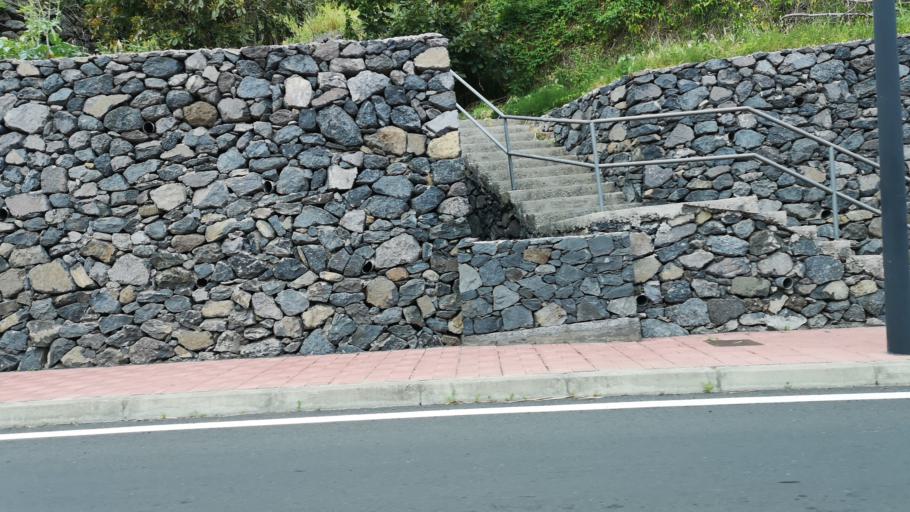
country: ES
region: Canary Islands
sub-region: Provincia de Santa Cruz de Tenerife
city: Hermigua
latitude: 28.1595
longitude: -17.1984
